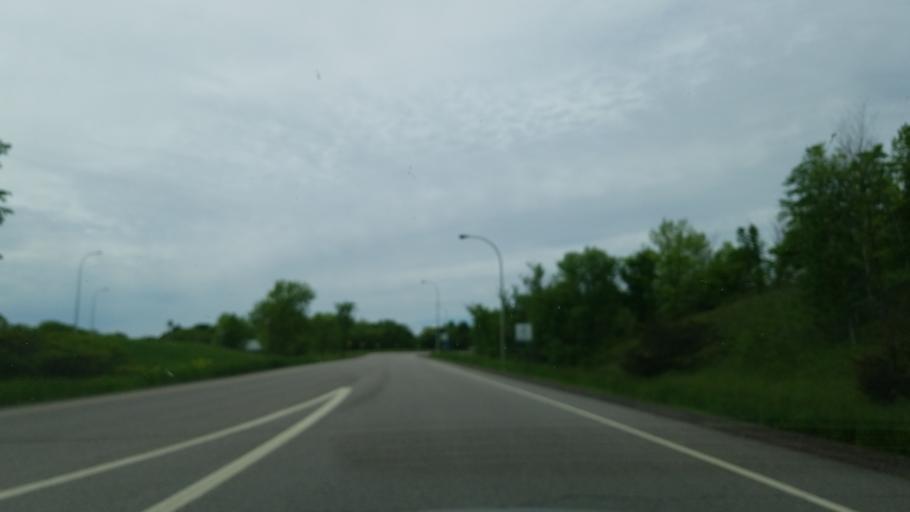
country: US
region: Minnesota
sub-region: Stearns County
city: Avon
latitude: 45.6056
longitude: -94.4789
